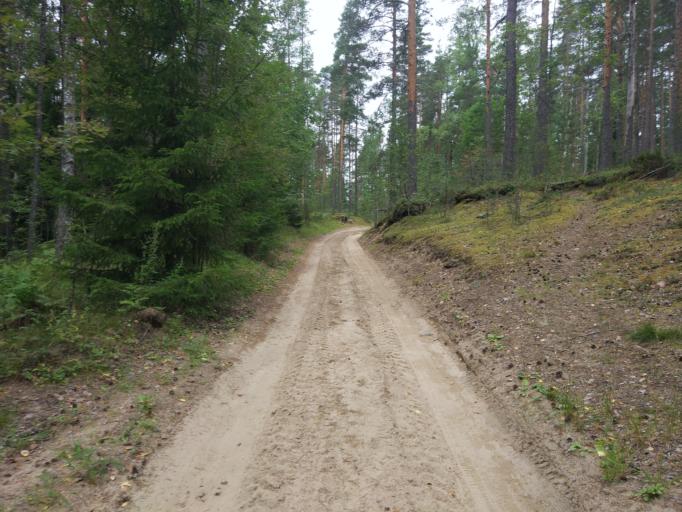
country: RU
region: Leningrad
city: Kuznechnoye
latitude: 61.0118
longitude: 29.6453
